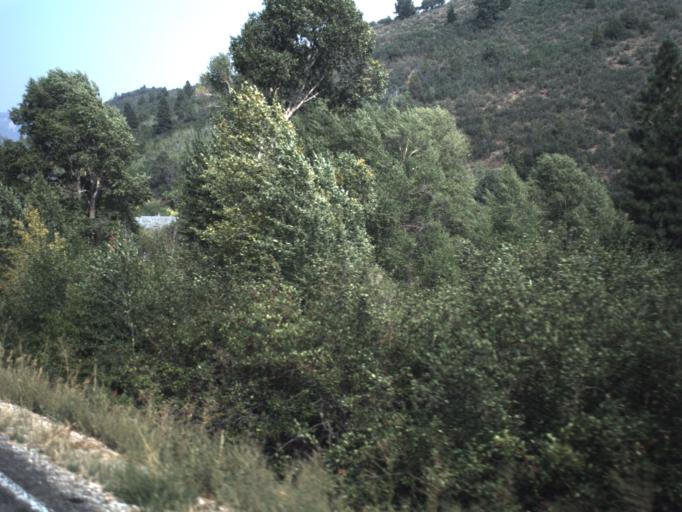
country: US
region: Utah
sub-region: Summit County
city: Francis
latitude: 40.6198
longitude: -111.2061
